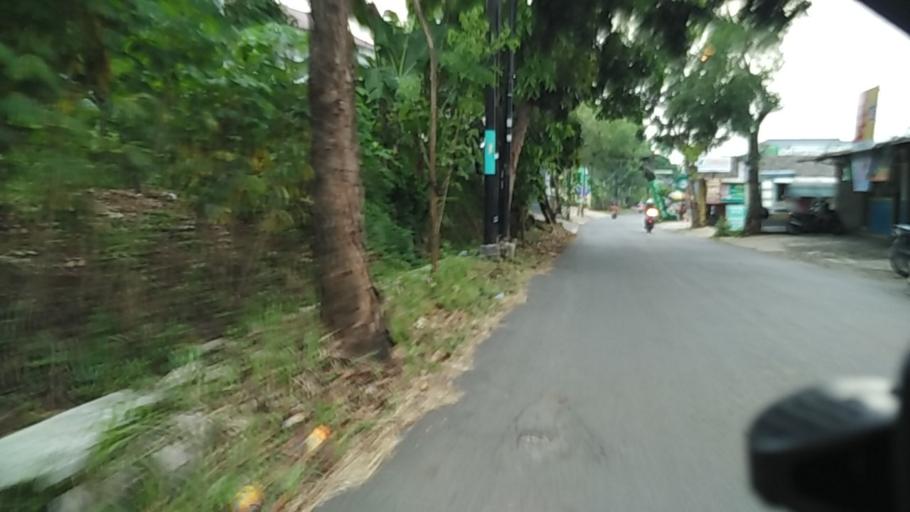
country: ID
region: Central Java
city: Semarang
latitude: -7.0606
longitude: 110.4356
